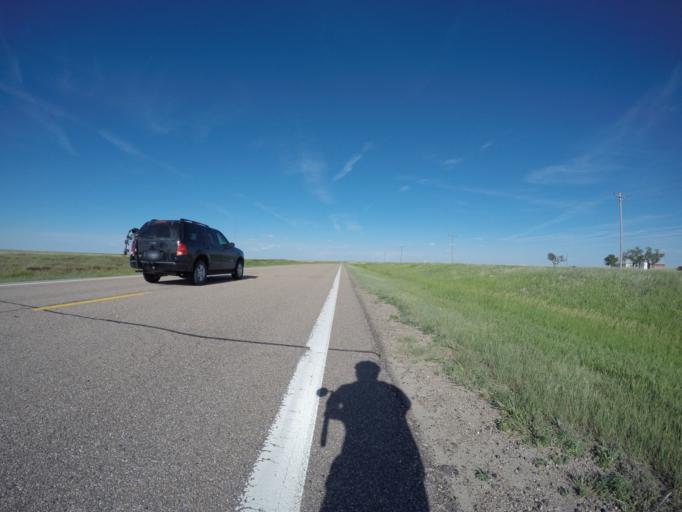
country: US
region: Kansas
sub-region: Cheyenne County
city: Saint Francis
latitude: 39.7565
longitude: -101.9873
